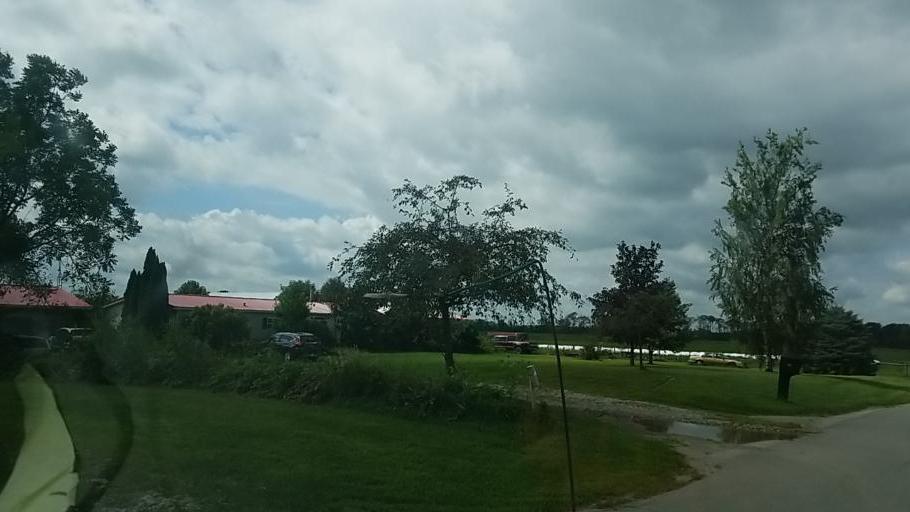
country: US
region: Ohio
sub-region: Madison County
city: Bethel
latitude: 39.6917
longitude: -83.4558
